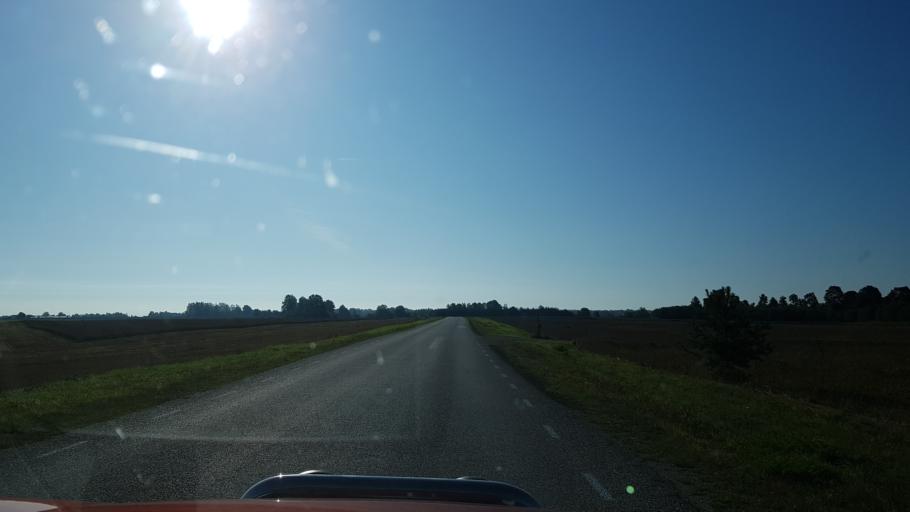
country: EE
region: Jogevamaa
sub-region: Tabivere vald
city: Tabivere
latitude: 58.6793
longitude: 26.6651
